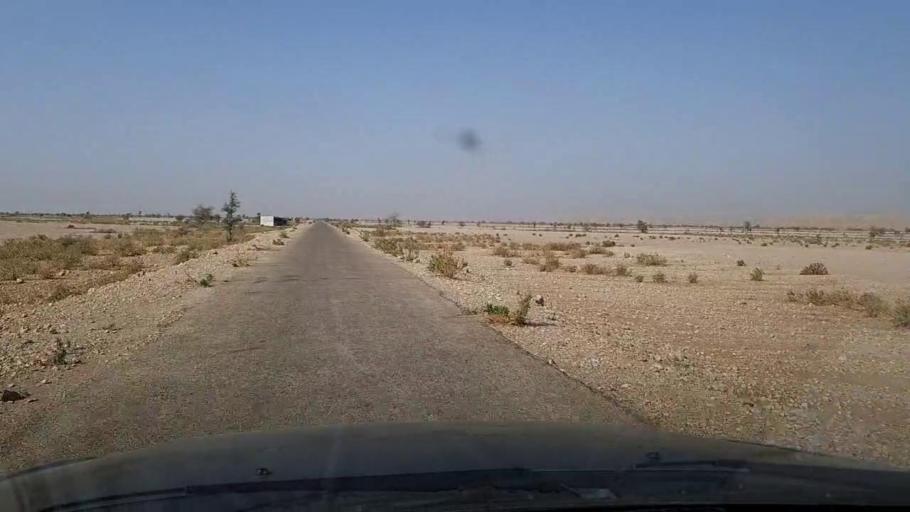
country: PK
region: Sindh
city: Sann
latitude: 25.9038
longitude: 68.0020
